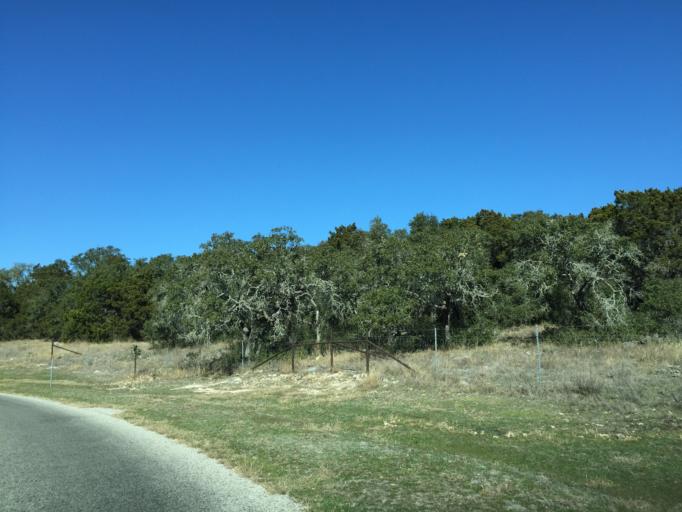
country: US
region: Texas
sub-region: Comal County
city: Garden Ridge
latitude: 29.6936
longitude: -98.3395
